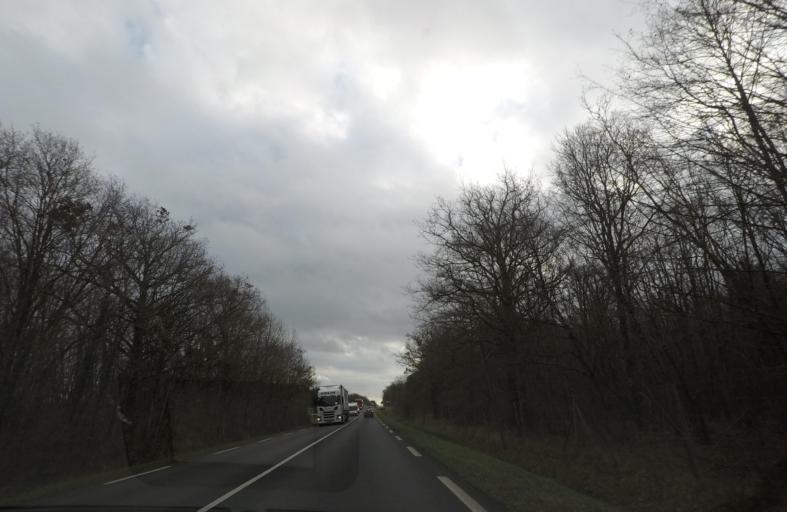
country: FR
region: Centre
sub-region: Departement du Loir-et-Cher
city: Soings-en-Sologne
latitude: 47.4568
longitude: 1.5263
